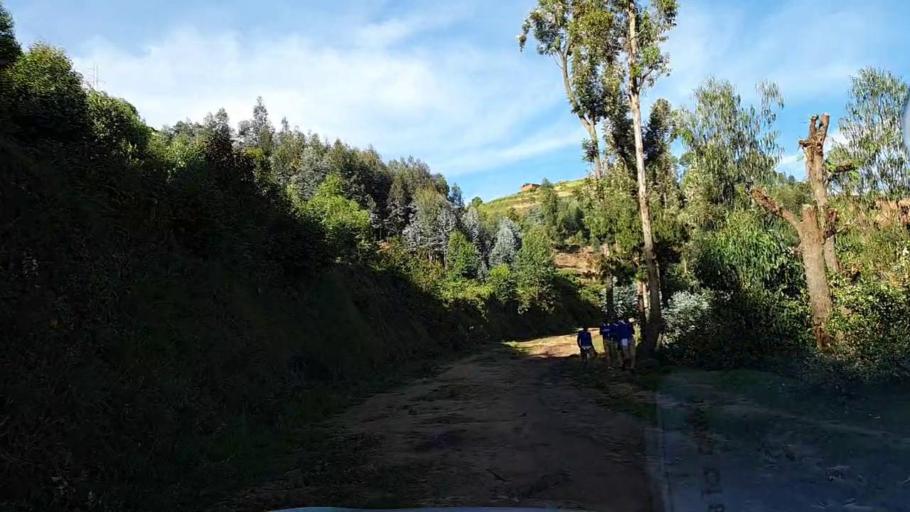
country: RW
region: Southern Province
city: Gikongoro
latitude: -2.4139
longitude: 29.5162
